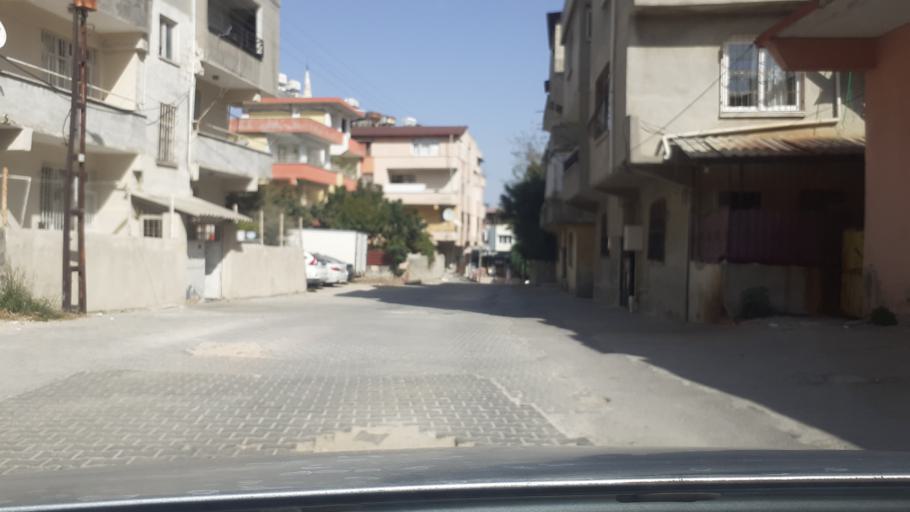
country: TR
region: Hatay
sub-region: Antakya Ilcesi
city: Antakya
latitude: 36.2113
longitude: 36.1517
